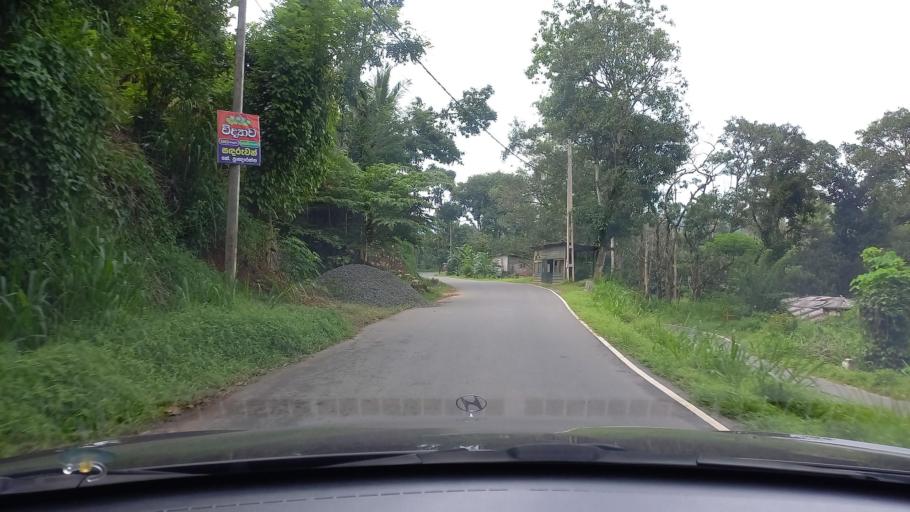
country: LK
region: Central
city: Gampola
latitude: 7.2129
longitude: 80.6150
